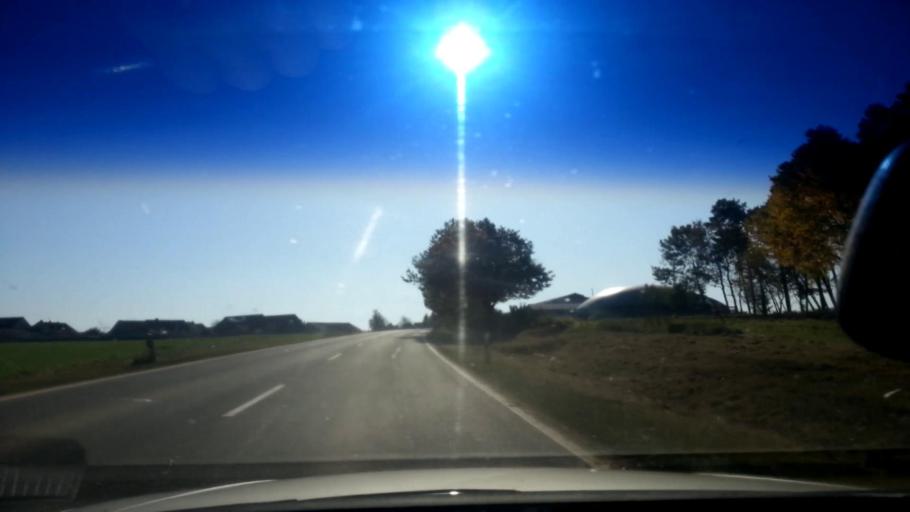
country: DE
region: Bavaria
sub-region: Upper Franconia
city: Stadelhofen
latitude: 49.9897
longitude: 11.2263
